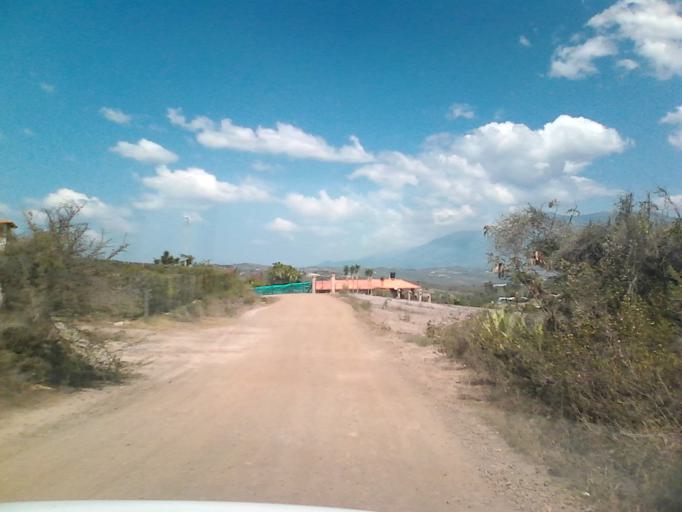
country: CO
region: Boyaca
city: Villa de Leiva
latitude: 5.6281
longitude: -73.5840
